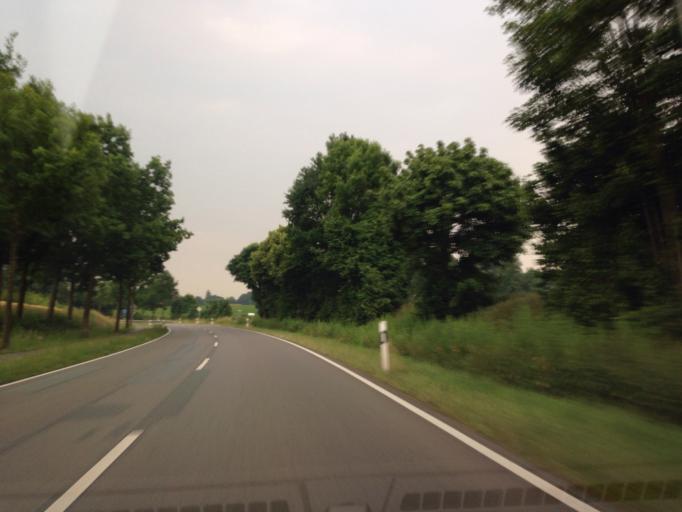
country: DE
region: North Rhine-Westphalia
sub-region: Regierungsbezirk Munster
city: Havixbeck
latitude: 51.9489
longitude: 7.4318
